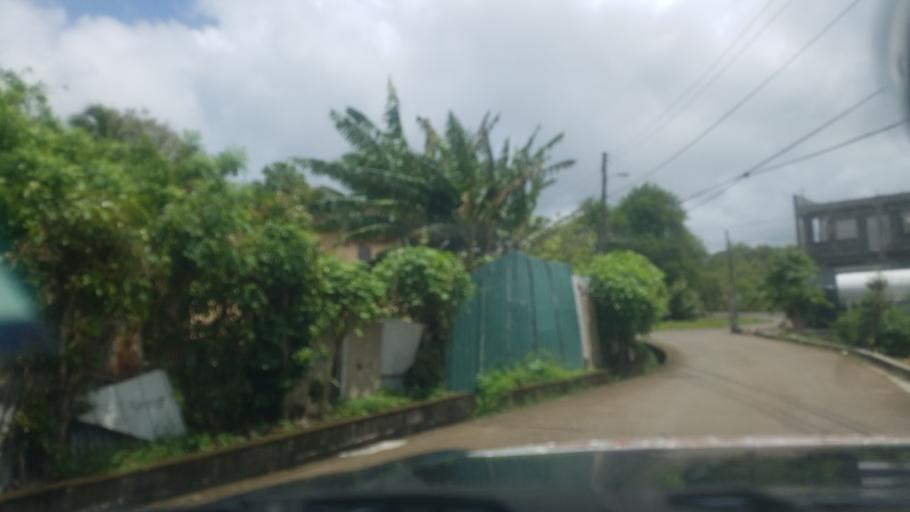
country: LC
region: Laborie Quarter
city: Laborie
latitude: 13.7500
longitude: -60.9687
